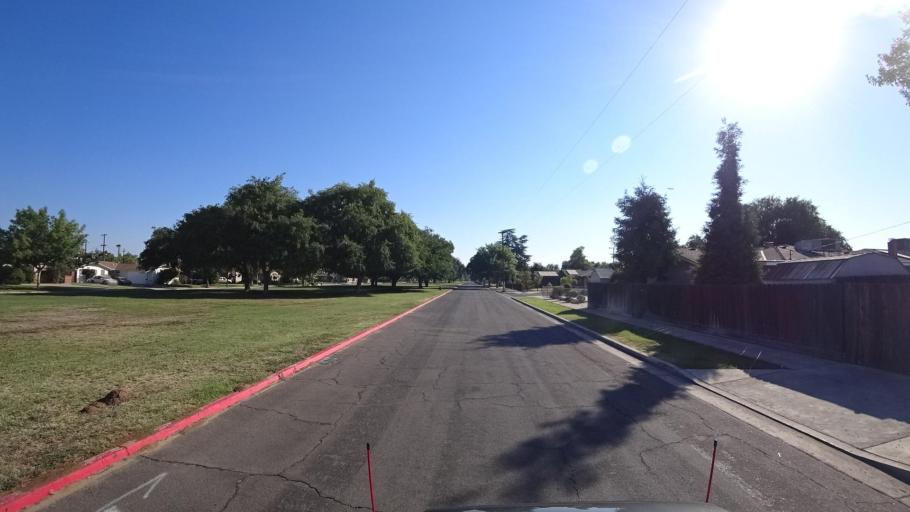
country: US
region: California
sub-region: Fresno County
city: Fresno
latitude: 36.7889
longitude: -119.7665
